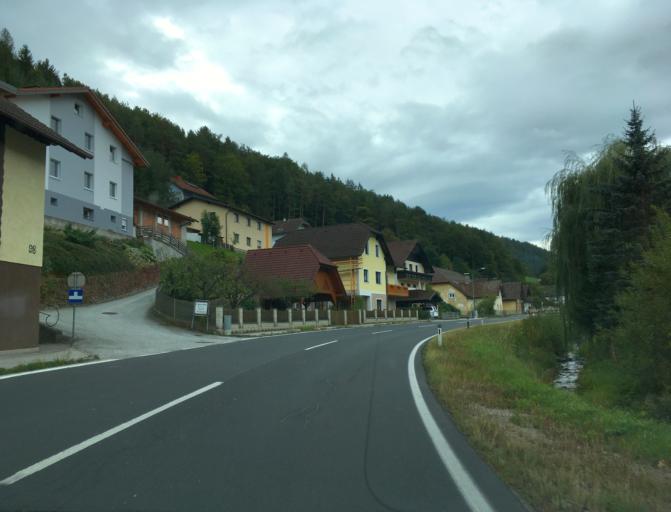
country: AT
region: Lower Austria
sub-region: Politischer Bezirk Neunkirchen
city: Edlitz
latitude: 47.5884
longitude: 16.1469
